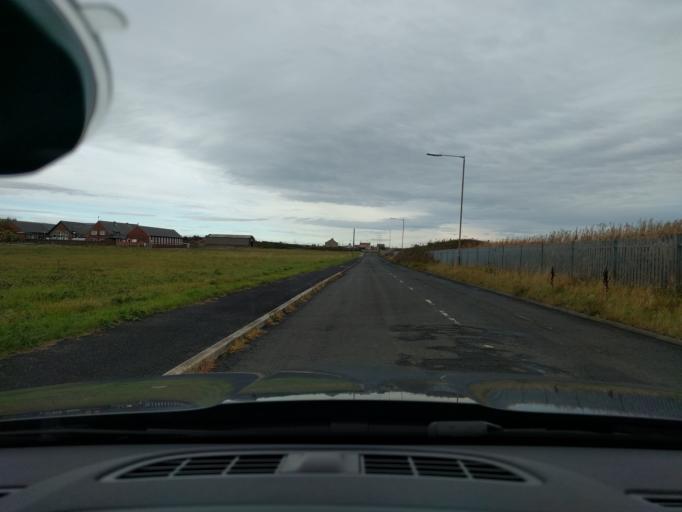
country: GB
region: England
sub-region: Northumberland
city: Blyth
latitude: 55.1469
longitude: -1.5217
